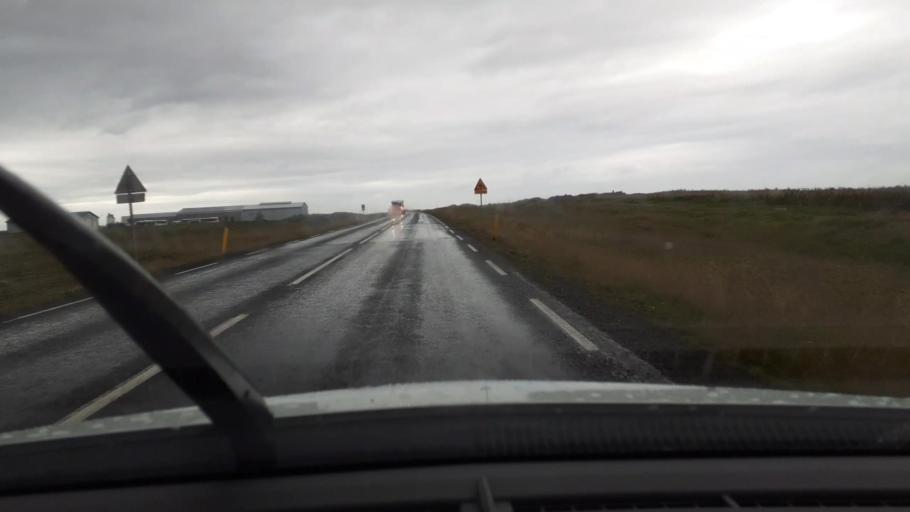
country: IS
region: West
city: Akranes
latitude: 64.3422
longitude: -22.0163
